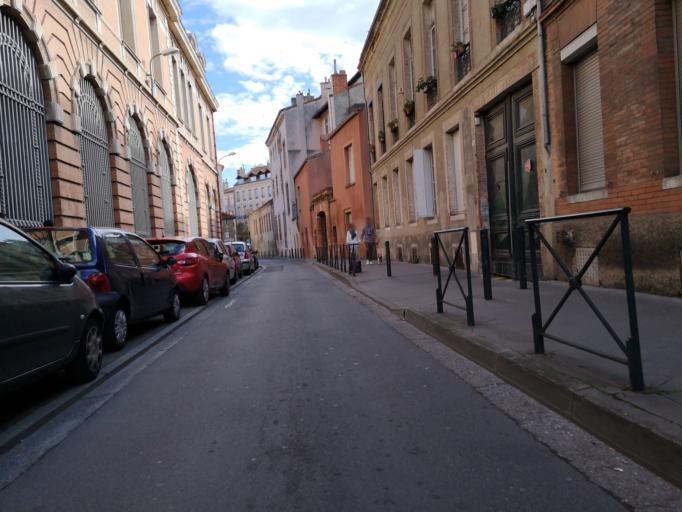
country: FR
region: Midi-Pyrenees
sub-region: Departement de la Haute-Garonne
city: Toulouse
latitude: 43.6053
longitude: 1.4400
